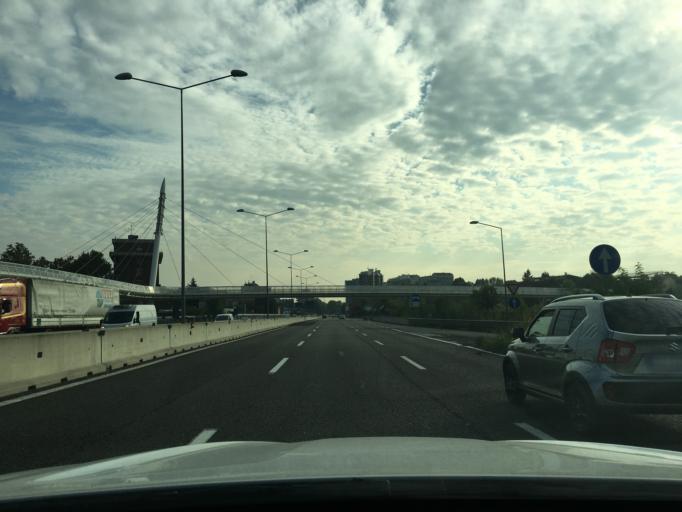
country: IT
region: Lombardy
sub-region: Citta metropolitana di Milano
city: Cinisello Balsamo
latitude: 45.5561
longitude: 9.2399
